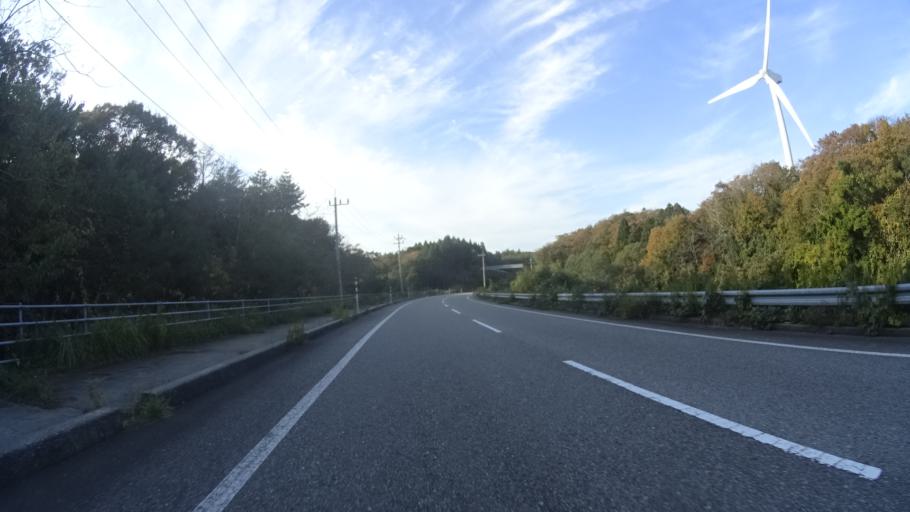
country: JP
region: Ishikawa
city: Hakui
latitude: 37.0741
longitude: 136.7317
